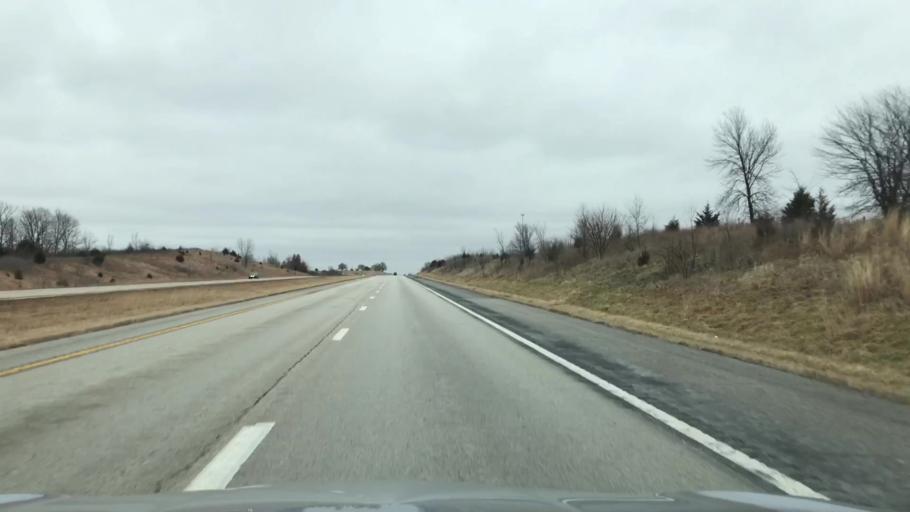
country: US
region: Missouri
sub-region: Caldwell County
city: Hamilton
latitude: 39.7491
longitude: -94.0681
